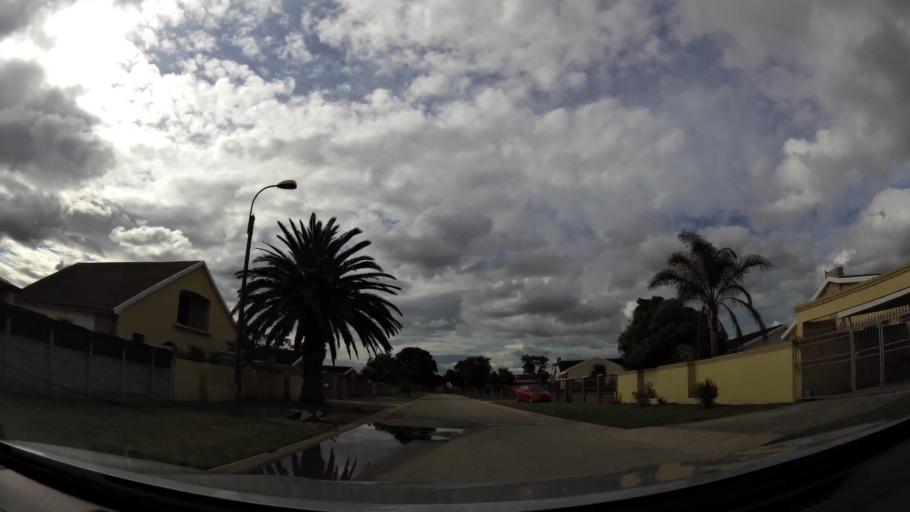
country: ZA
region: Eastern Cape
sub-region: Nelson Mandela Bay Metropolitan Municipality
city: Port Elizabeth
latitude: -33.9343
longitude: 25.5072
